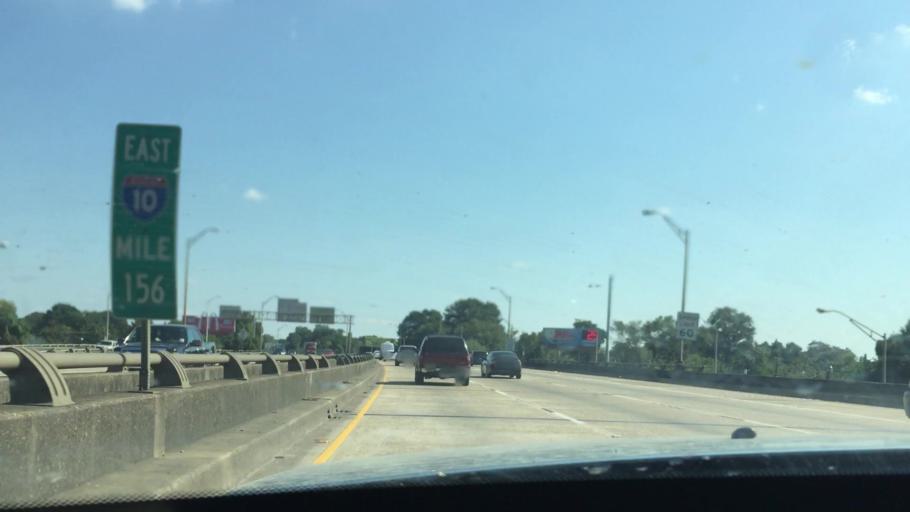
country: US
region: Louisiana
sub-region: East Baton Rouge Parish
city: Baton Rouge
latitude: 30.4327
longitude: -91.1755
